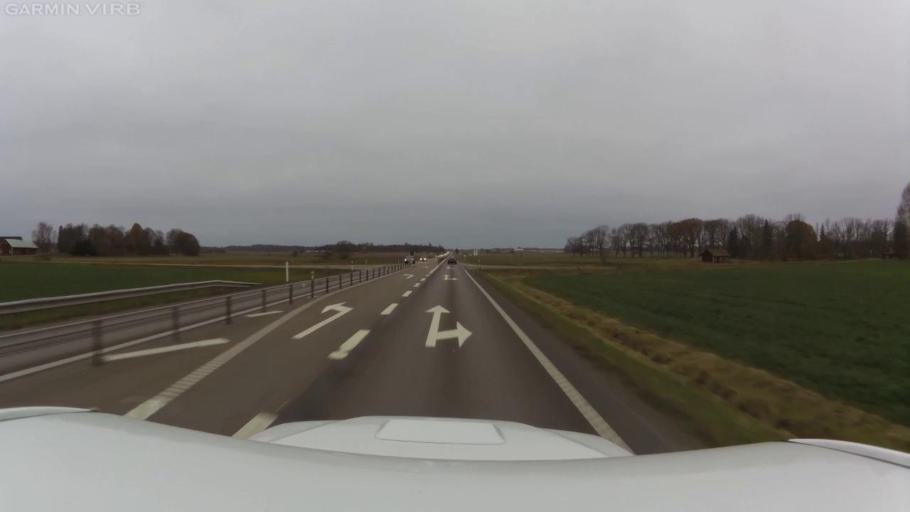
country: SE
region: OEstergoetland
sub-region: Linkopings Kommun
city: Vikingstad
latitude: 58.3750
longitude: 15.4742
